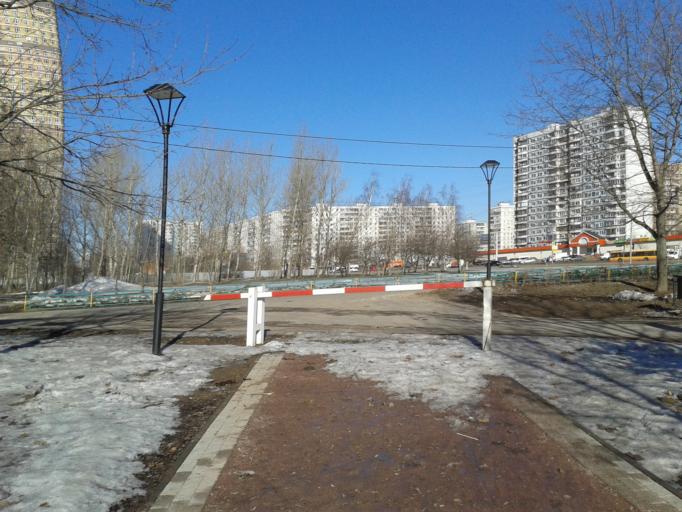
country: RU
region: Moscow
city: Strogino
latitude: 55.8032
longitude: 37.4194
